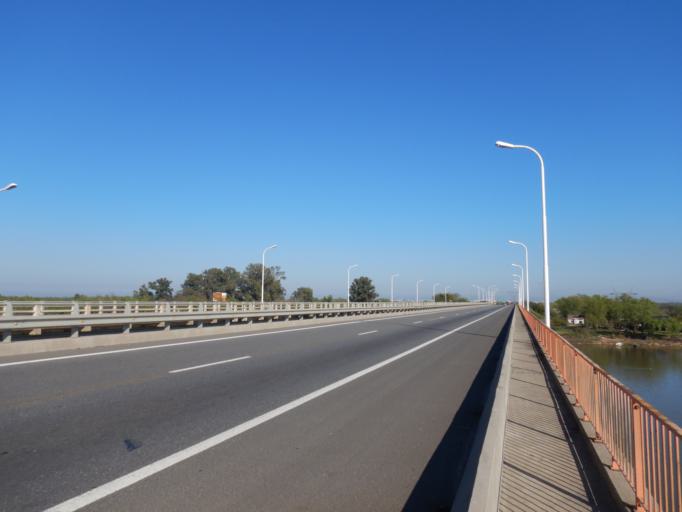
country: AR
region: Entre Rios
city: Parana
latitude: -31.6602
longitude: -60.5972
